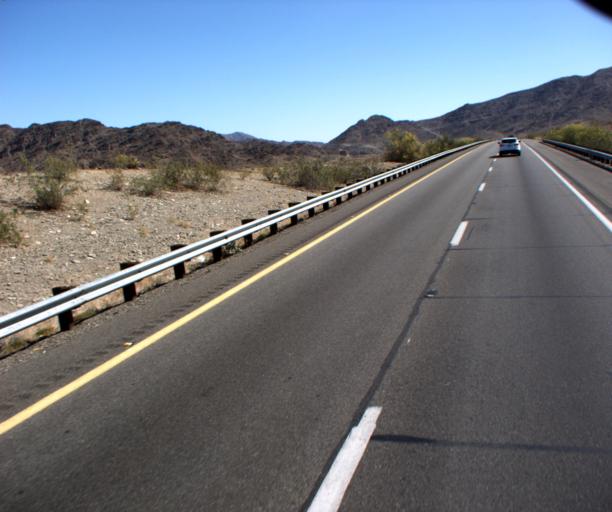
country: US
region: Arizona
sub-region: La Paz County
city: Ehrenberg
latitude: 33.6319
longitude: -114.4033
